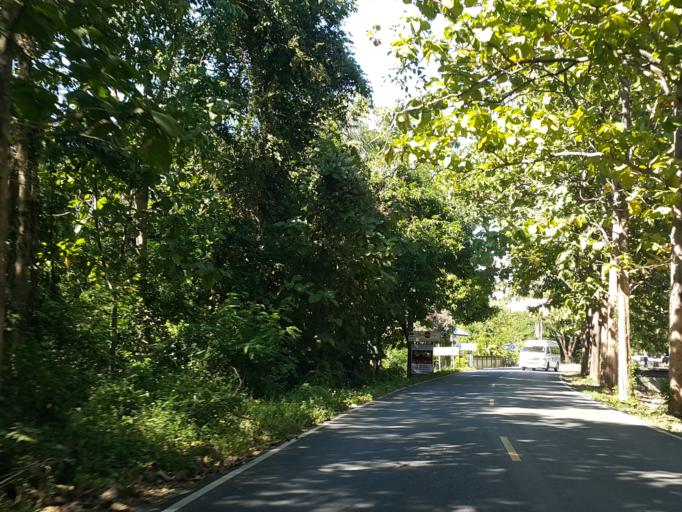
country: TH
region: Chiang Mai
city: San Sai
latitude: 18.8943
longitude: 99.1402
